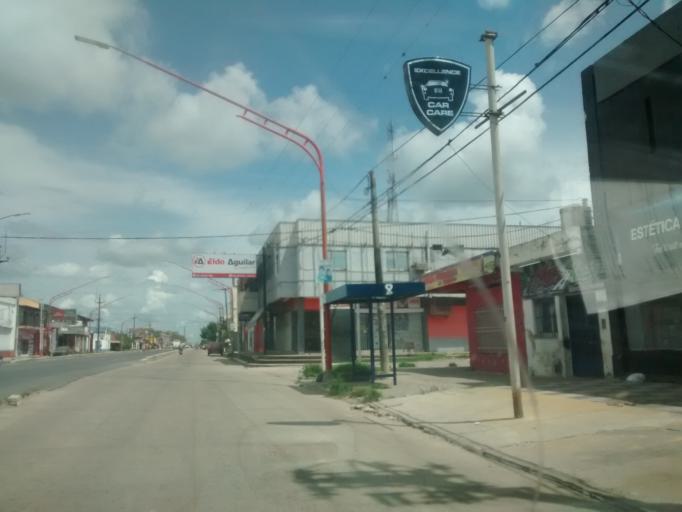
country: AR
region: Chaco
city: Resistencia
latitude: -27.4506
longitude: -59.0014
